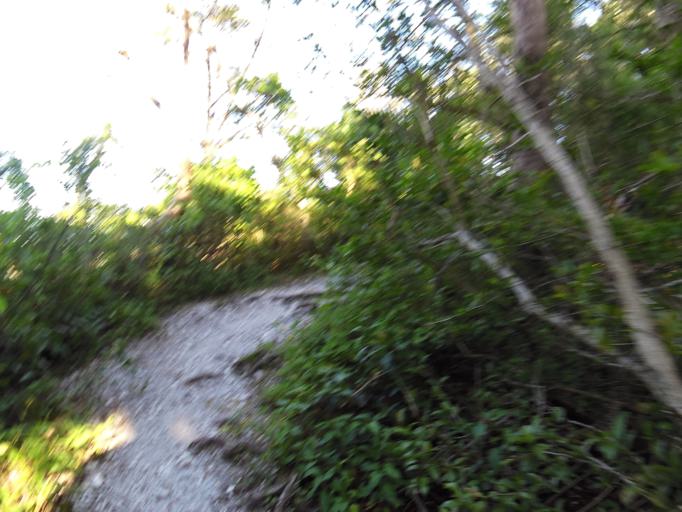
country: US
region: Florida
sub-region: Duval County
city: Atlantic Beach
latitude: 30.3804
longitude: -81.4815
